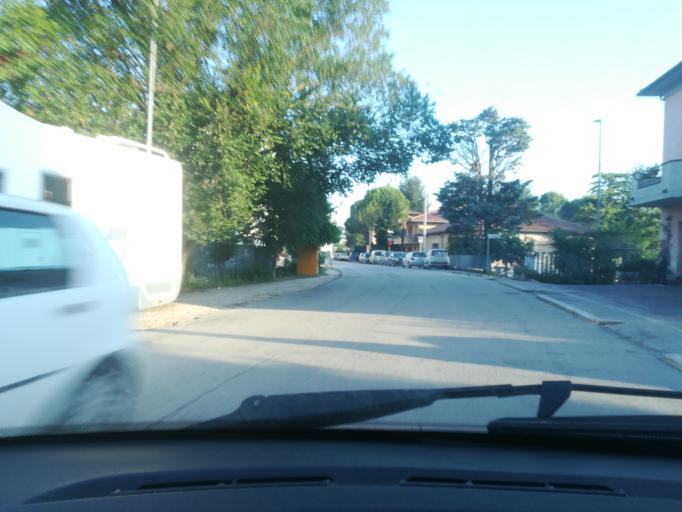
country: IT
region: The Marches
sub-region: Provincia di Macerata
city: Piediripa
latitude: 43.2764
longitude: 13.4840
